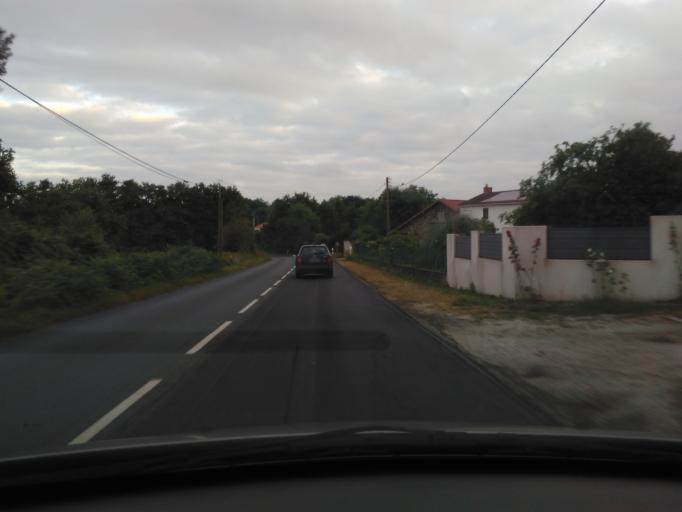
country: FR
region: Pays de la Loire
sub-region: Departement de la Vendee
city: Dompierre-sur-Yon
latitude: 46.7318
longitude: -1.3687
